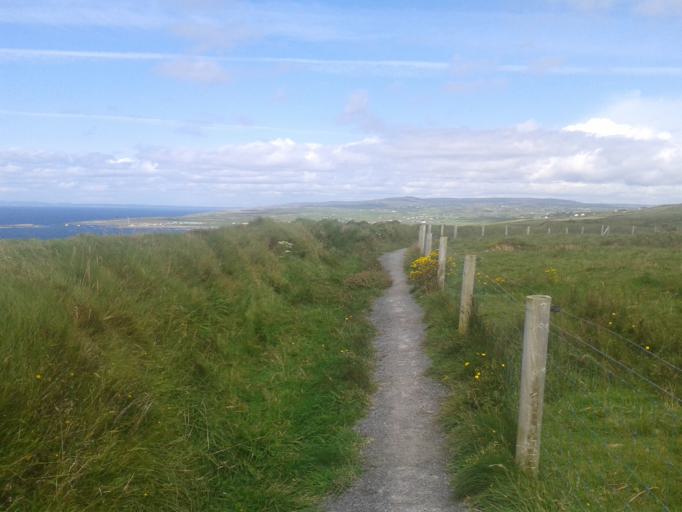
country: IE
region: Munster
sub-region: An Clar
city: Kilrush
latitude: 52.9882
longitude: -9.4203
